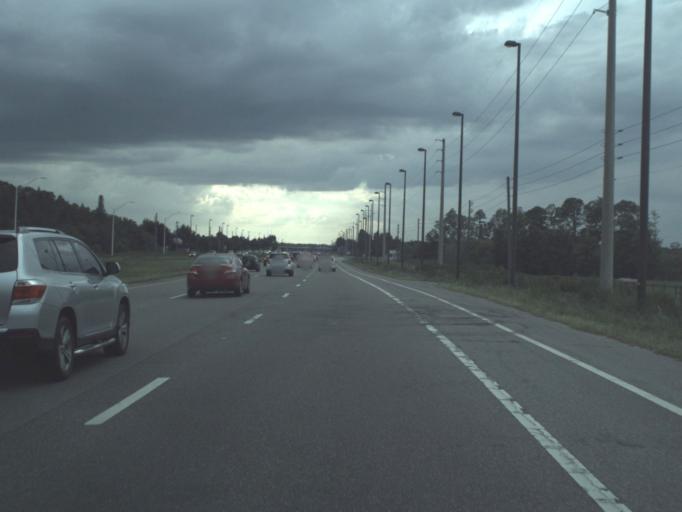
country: US
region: Florida
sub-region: Hillsborough County
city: Cheval
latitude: 28.1934
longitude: -82.5353
